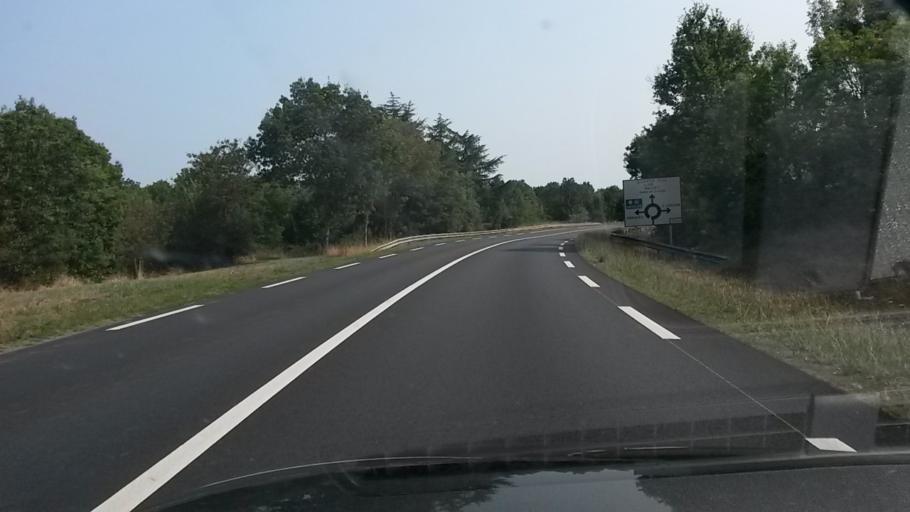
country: FR
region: Pays de la Loire
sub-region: Departement de la Loire-Atlantique
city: Ancenis
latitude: 47.3752
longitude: -1.1679
